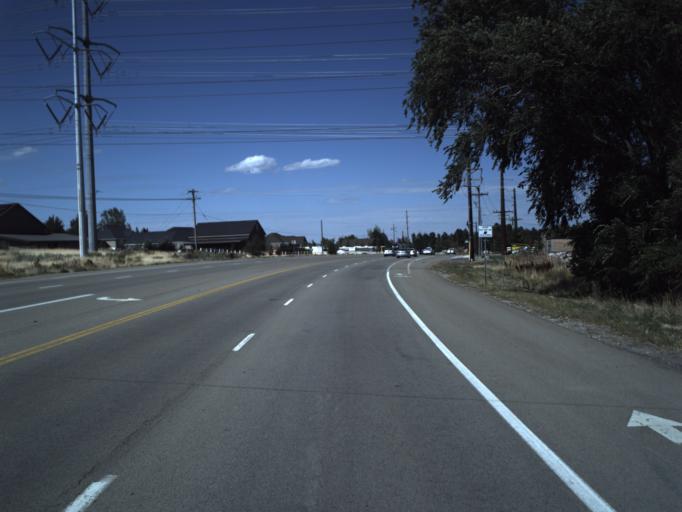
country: US
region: Utah
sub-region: Salt Lake County
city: Bluffdale
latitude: 40.4704
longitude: -111.9463
